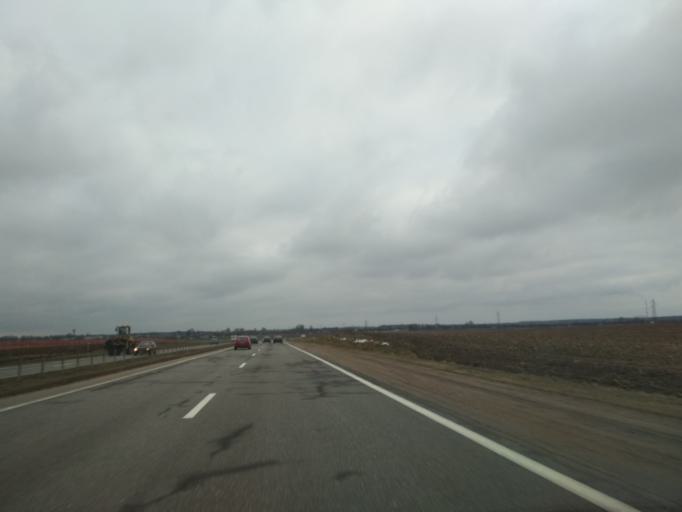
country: BY
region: Minsk
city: Dukora
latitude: 53.6803
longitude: 27.9229
